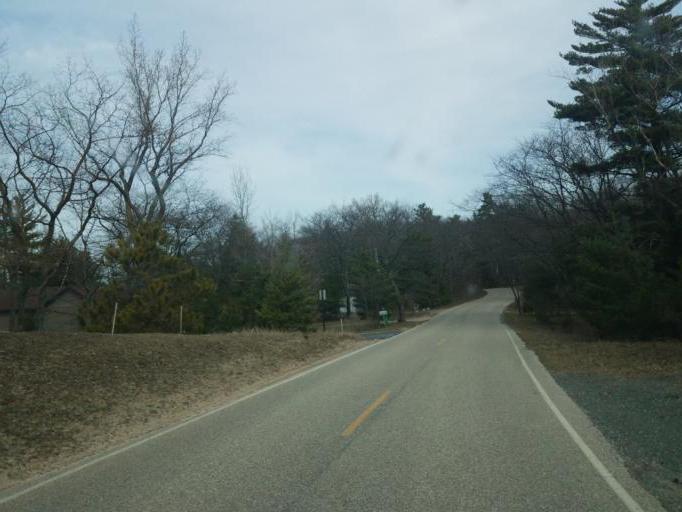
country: US
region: Michigan
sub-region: Oceana County
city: Hart
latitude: 43.6537
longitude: -86.5383
